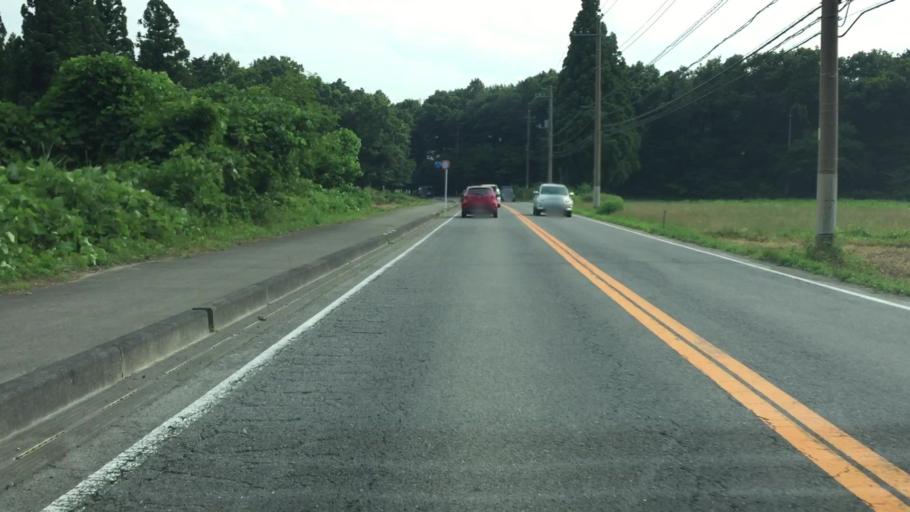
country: JP
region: Tochigi
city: Kuroiso
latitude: 36.9972
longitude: 139.9430
